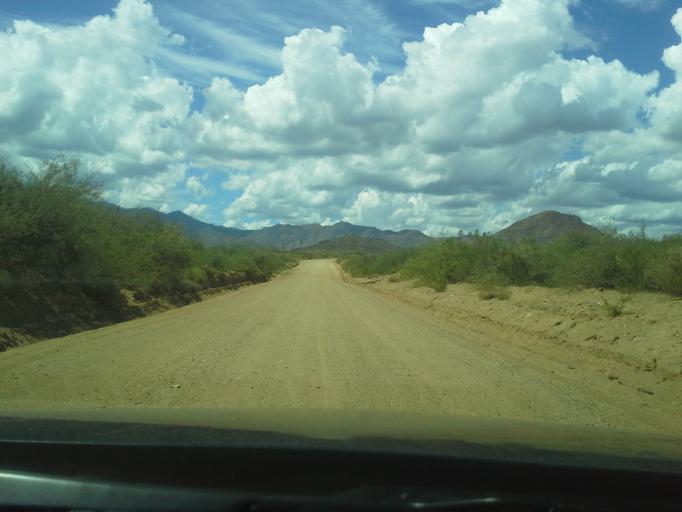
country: US
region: Arizona
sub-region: Yavapai County
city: Spring Valley
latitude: 34.2657
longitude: -112.1864
